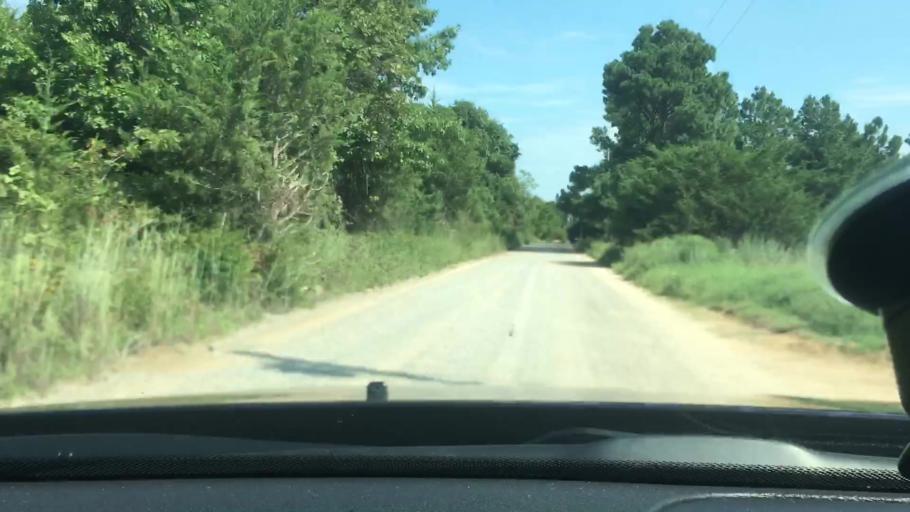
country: US
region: Texas
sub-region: Grayson County
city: Preston
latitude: 33.8928
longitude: -96.5626
